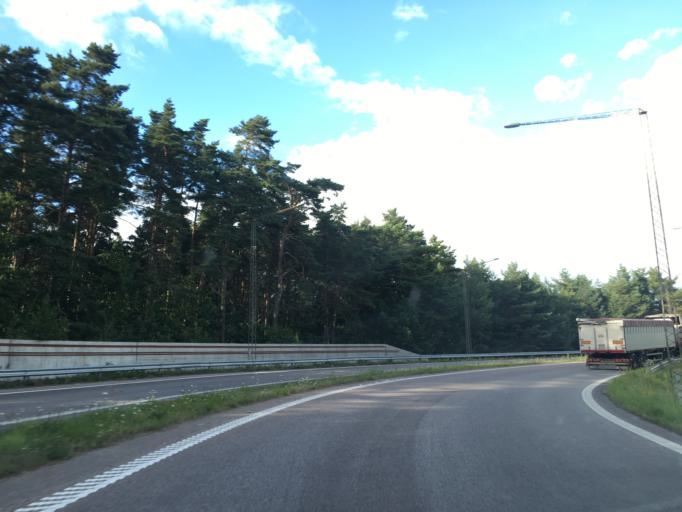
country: SE
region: Kalmar
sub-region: Kalmar Kommun
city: Kalmar
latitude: 56.6852
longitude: 16.3533
